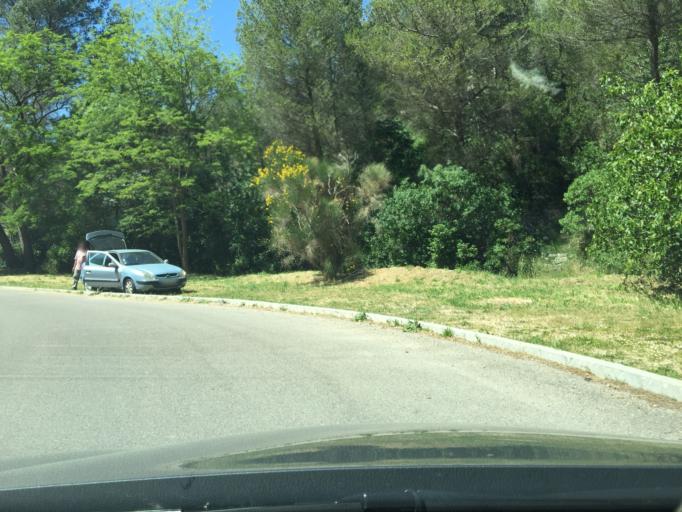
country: FR
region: Provence-Alpes-Cote d'Azur
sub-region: Departement des Bouches-du-Rhone
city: La Penne-sur-Huveaune
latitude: 43.2807
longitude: 5.4822
